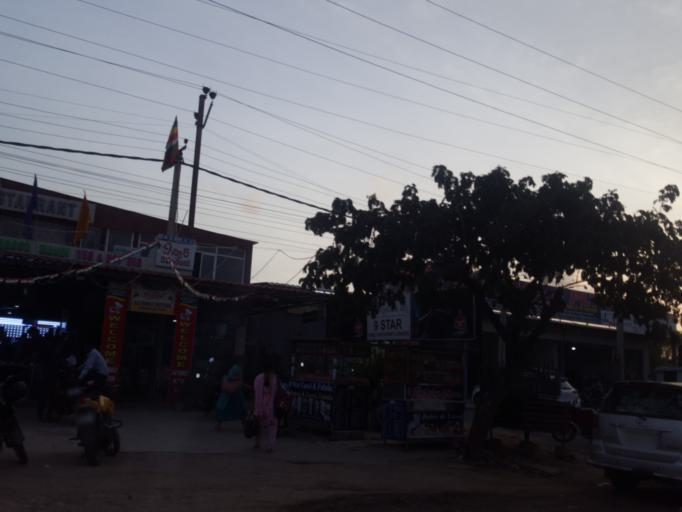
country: IN
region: Telangana
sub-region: Rangareddi
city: Kukatpalli
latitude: 17.5401
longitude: 78.3661
